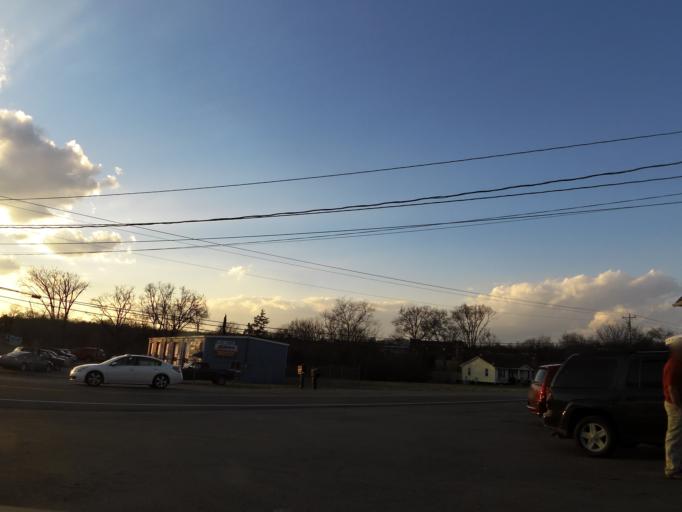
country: US
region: Tennessee
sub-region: Wilson County
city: Mount Juliet
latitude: 36.2320
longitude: -86.4910
